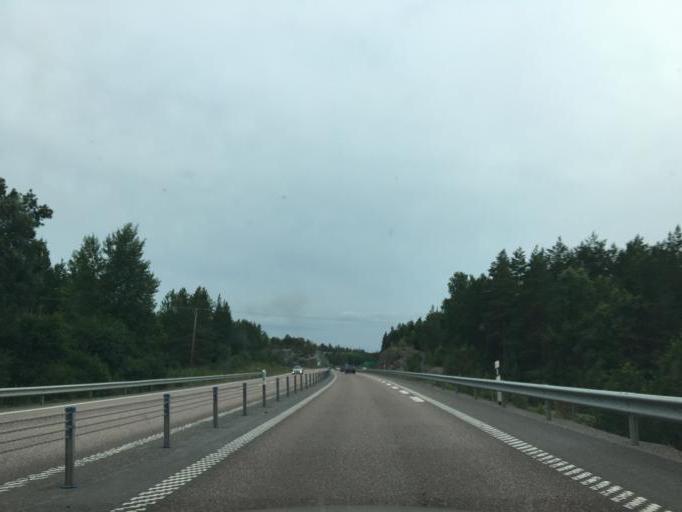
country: SE
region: Soedermanland
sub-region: Strangnas Kommun
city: Strangnas
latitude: 59.3716
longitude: 16.9602
